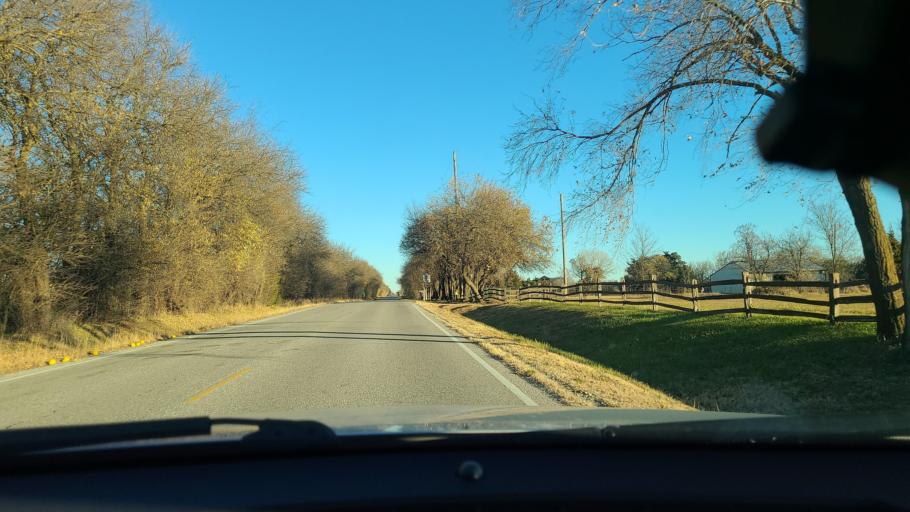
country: US
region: Kansas
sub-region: Sedgwick County
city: Park City
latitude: 37.8495
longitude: -97.3174
